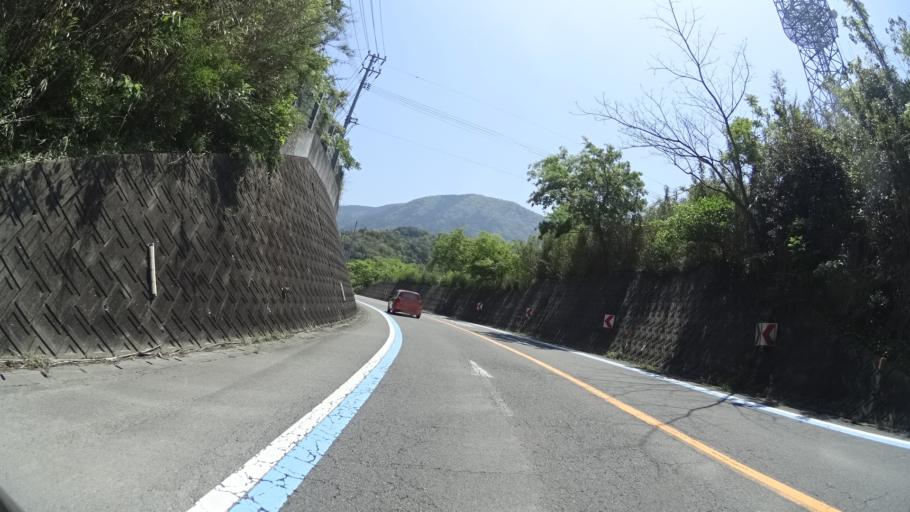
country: JP
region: Ehime
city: Iyo
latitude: 33.7119
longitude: 132.6682
